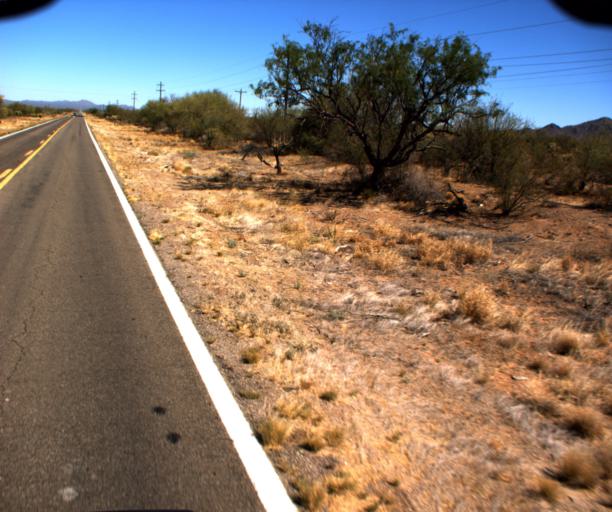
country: US
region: Arizona
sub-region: Pima County
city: Sells
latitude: 32.0120
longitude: -111.9948
